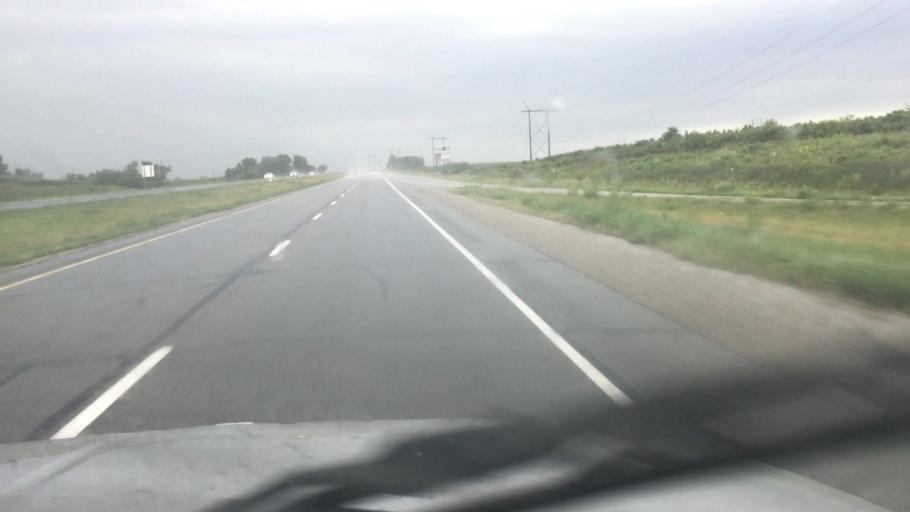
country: US
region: Iowa
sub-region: Washington County
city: Washington
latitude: 41.3343
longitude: -91.5522
